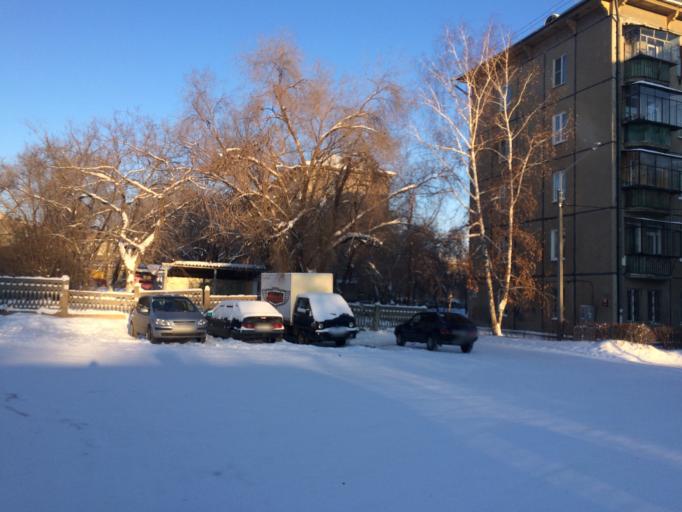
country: RU
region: Chelyabinsk
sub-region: Gorod Magnitogorsk
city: Magnitogorsk
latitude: 53.4150
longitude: 58.9890
